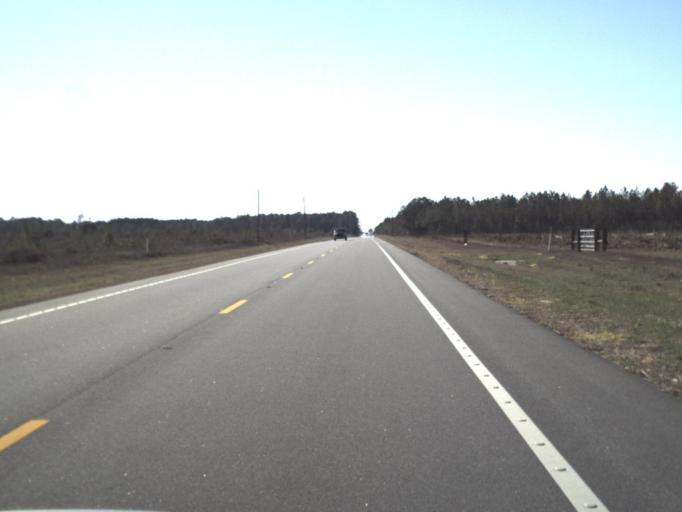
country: US
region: Florida
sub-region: Calhoun County
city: Blountstown
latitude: 30.4336
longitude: -85.2401
